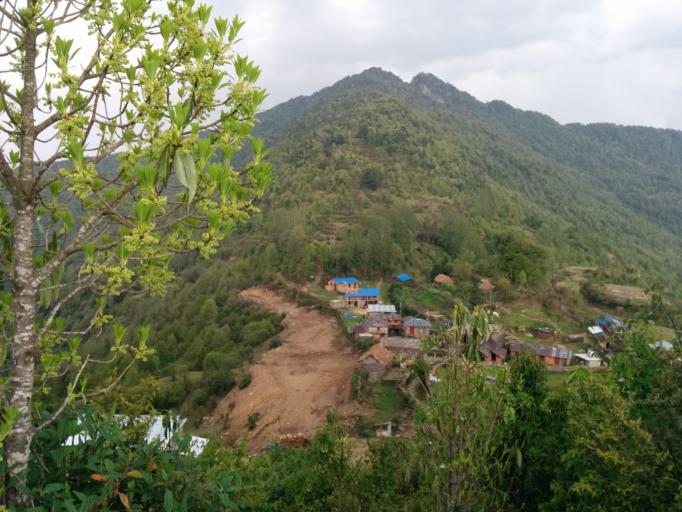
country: NP
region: Western Region
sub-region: Gandaki Zone
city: Pokhara
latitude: 28.2177
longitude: 83.8120
